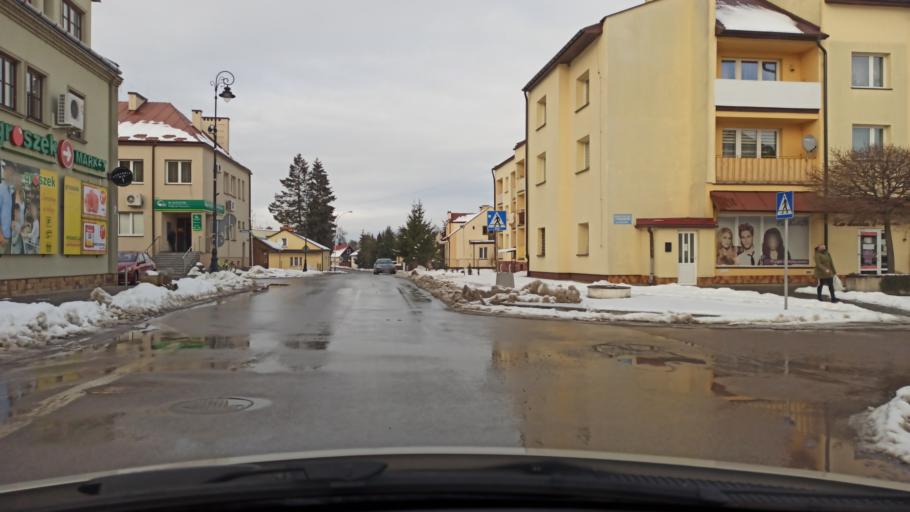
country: PL
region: Subcarpathian Voivodeship
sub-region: Powiat przeworski
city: Sieniawa
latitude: 50.1786
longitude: 22.6088
